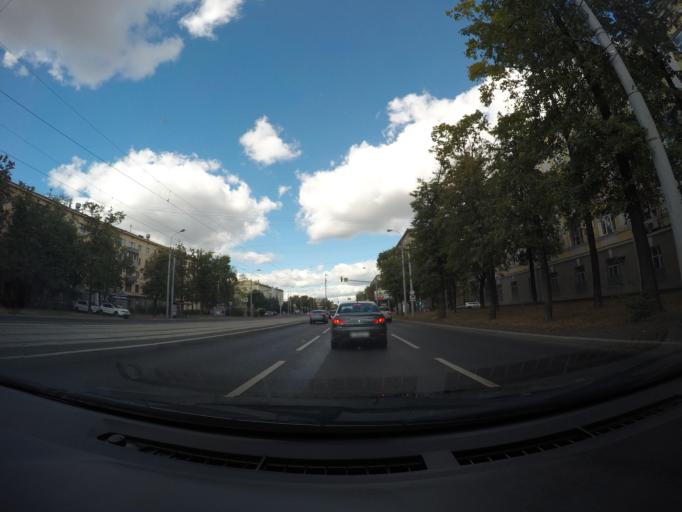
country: RU
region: Moscow
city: Lefortovo
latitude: 55.7667
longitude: 37.7313
